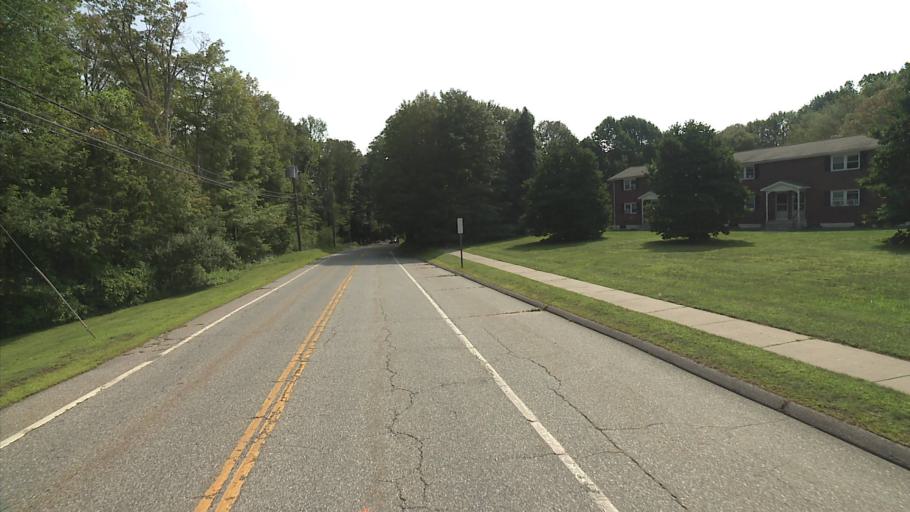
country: US
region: Connecticut
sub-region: New London County
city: Colchester
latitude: 41.5745
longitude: -72.3026
